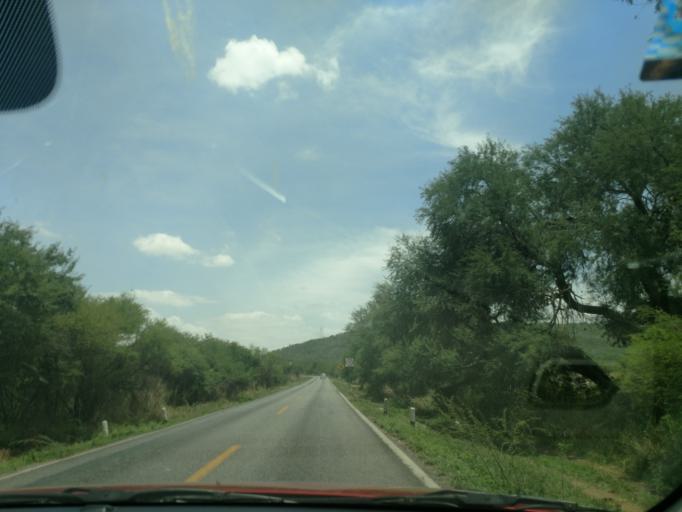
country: MX
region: San Luis Potosi
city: Ciudad Fernandez
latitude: 21.9962
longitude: -100.1383
